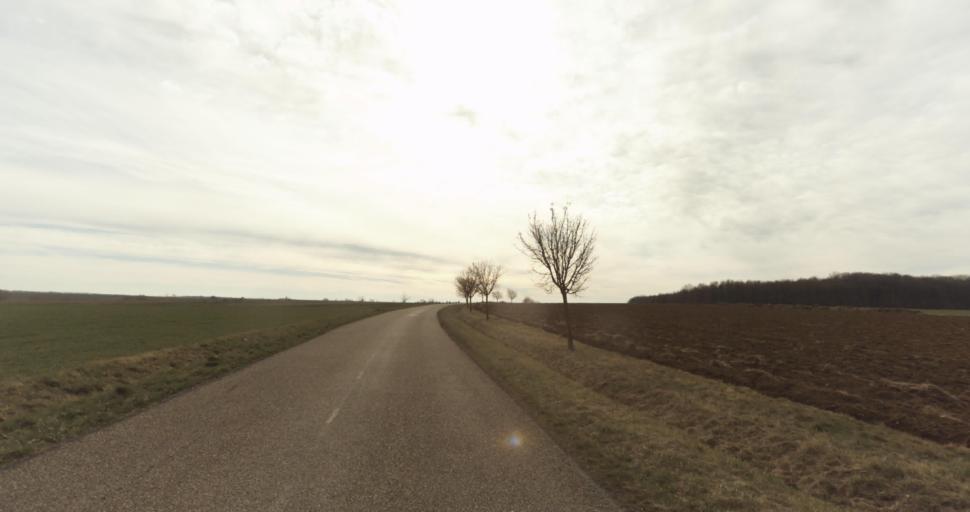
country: FR
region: Lorraine
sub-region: Departement de Meurthe-et-Moselle
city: Conflans-en-Jarnisy
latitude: 49.1390
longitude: 5.8506
